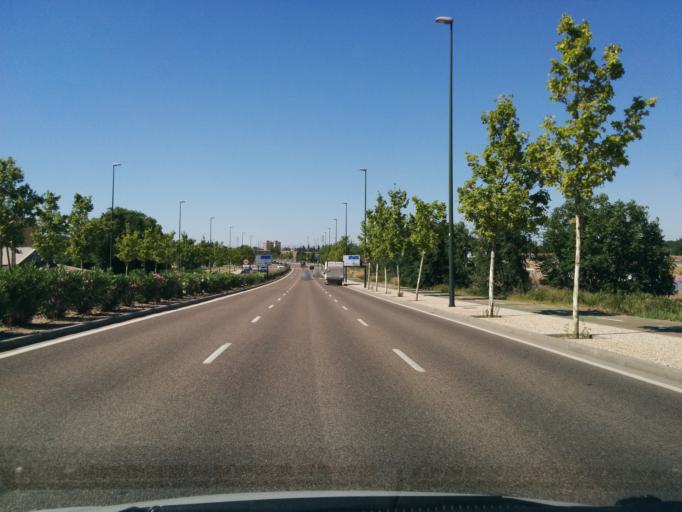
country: ES
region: Aragon
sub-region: Provincia de Zaragoza
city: Zaragoza
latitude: 41.6542
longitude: -0.8537
